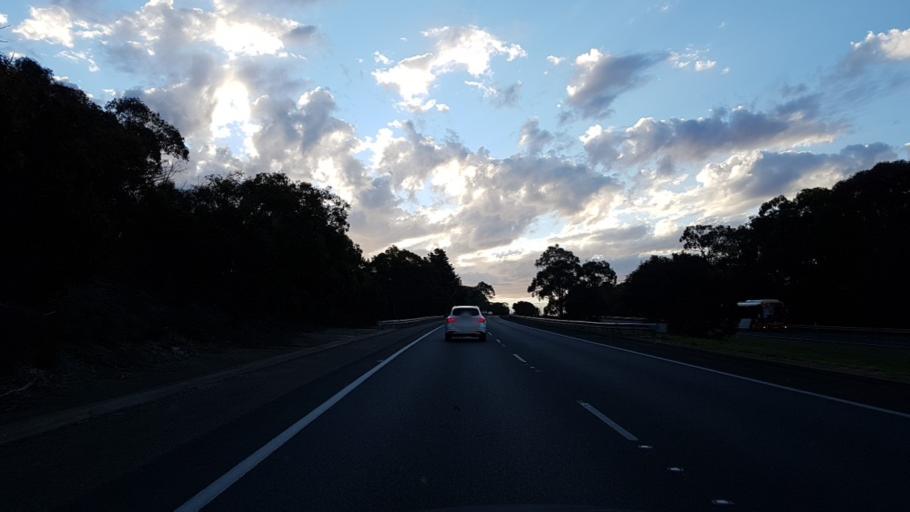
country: AU
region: South Australia
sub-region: Adelaide Hills
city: Bridgewater
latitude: -35.0066
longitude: 138.7743
